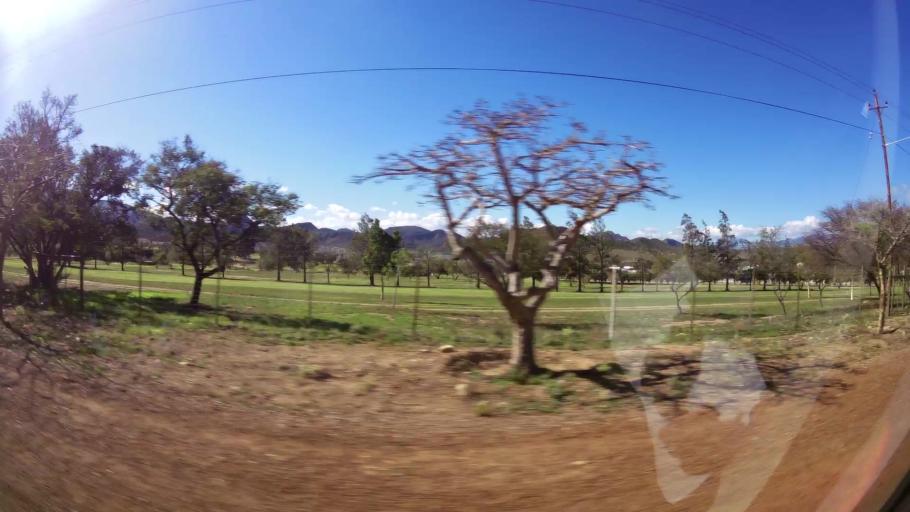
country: ZA
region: Western Cape
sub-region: Cape Winelands District Municipality
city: Ashton
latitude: -33.7740
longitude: 20.1323
